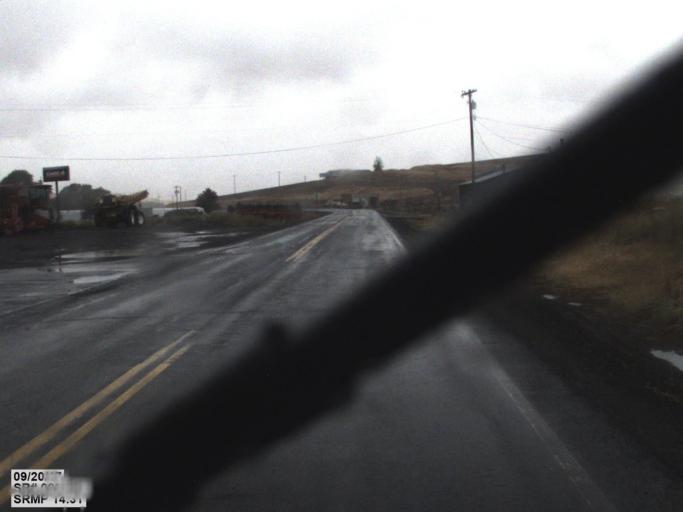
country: US
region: Washington
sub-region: Whitman County
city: Colfax
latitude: 47.0925
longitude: -117.5843
